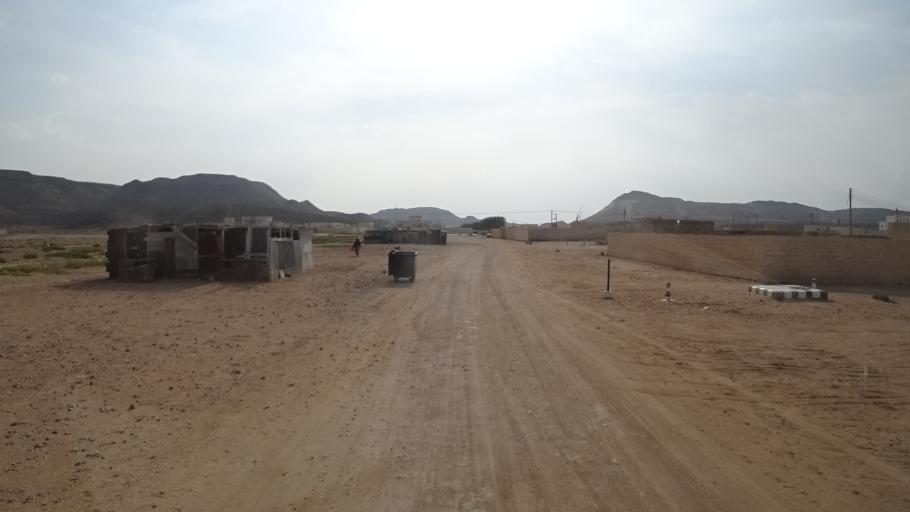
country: OM
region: Ash Sharqiyah
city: Sur
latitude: 22.4325
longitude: 59.8270
